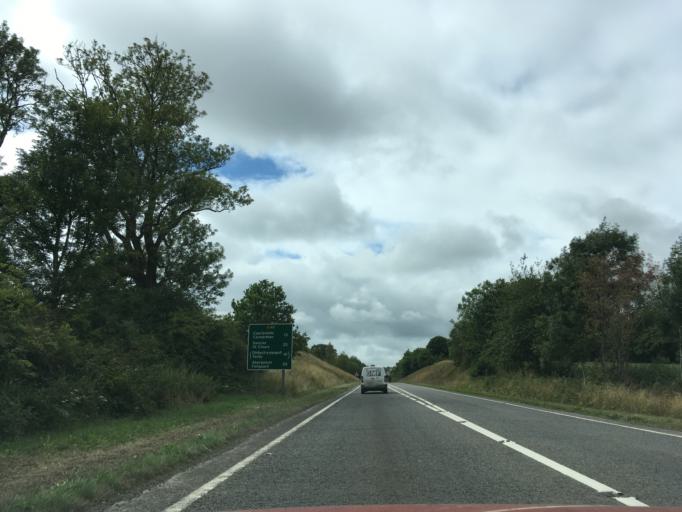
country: GB
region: Wales
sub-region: Carmarthenshire
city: Llandeilo
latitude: 51.8911
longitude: -4.0145
